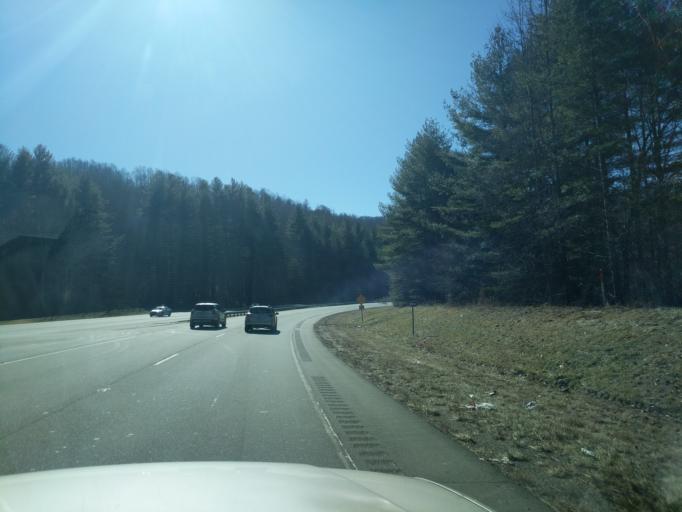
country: US
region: North Carolina
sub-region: Jackson County
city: Cullowhee
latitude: 35.4006
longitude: -83.1248
